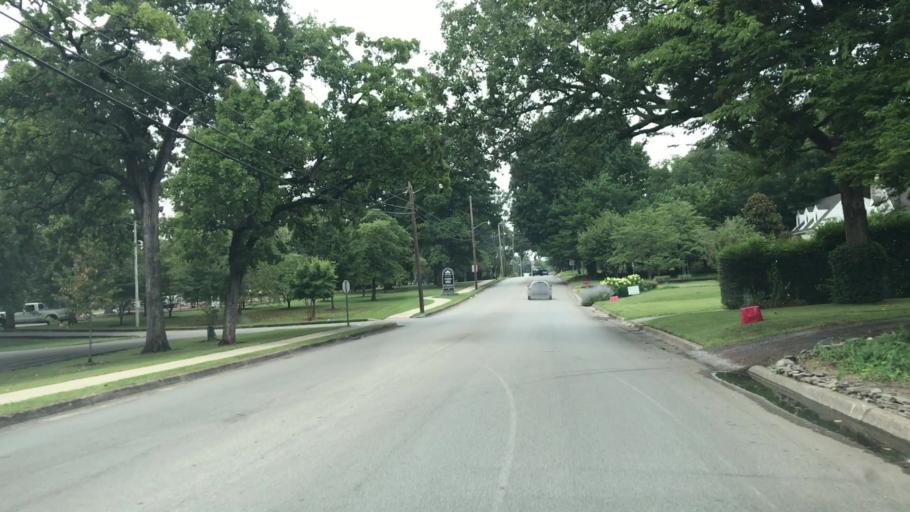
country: US
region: Kentucky
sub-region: Warren County
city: Bowling Green
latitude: 36.9803
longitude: -86.4341
